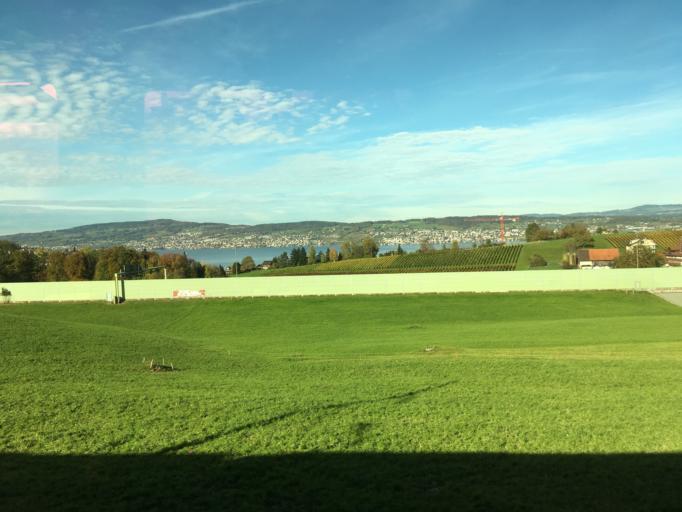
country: CH
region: Zurich
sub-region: Bezirk Horgen
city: Richterswil / Richterswil (Dorfkern)
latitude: 47.1951
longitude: 8.7066
